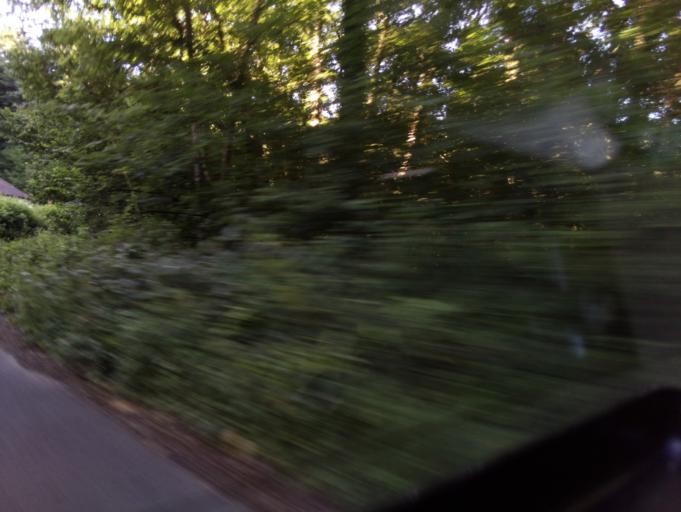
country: GB
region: Wales
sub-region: Monmouthshire
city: Tintern
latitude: 51.7168
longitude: -2.6885
